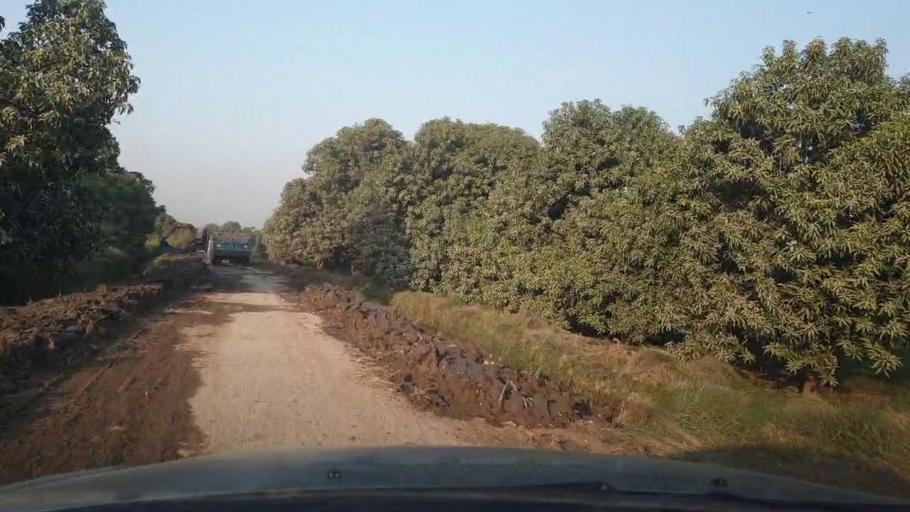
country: PK
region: Sindh
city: Tando Jam
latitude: 25.4222
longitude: 68.4932
